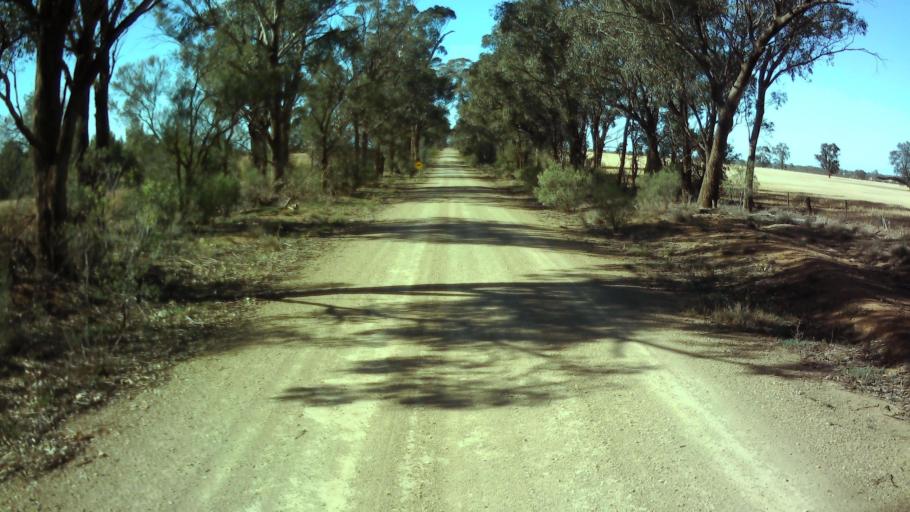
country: AU
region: New South Wales
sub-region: Weddin
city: Grenfell
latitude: -33.9038
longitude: 147.8780
